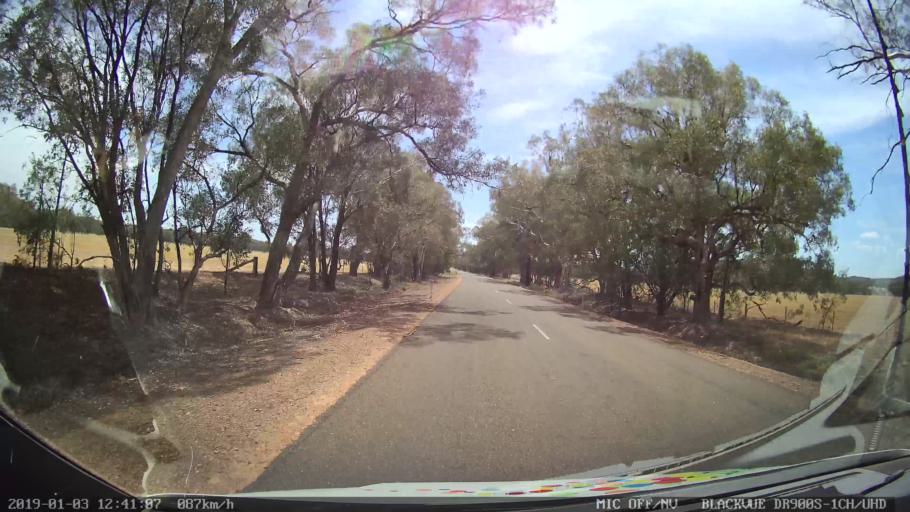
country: AU
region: New South Wales
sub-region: Weddin
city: Grenfell
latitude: -33.8039
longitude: 148.2144
